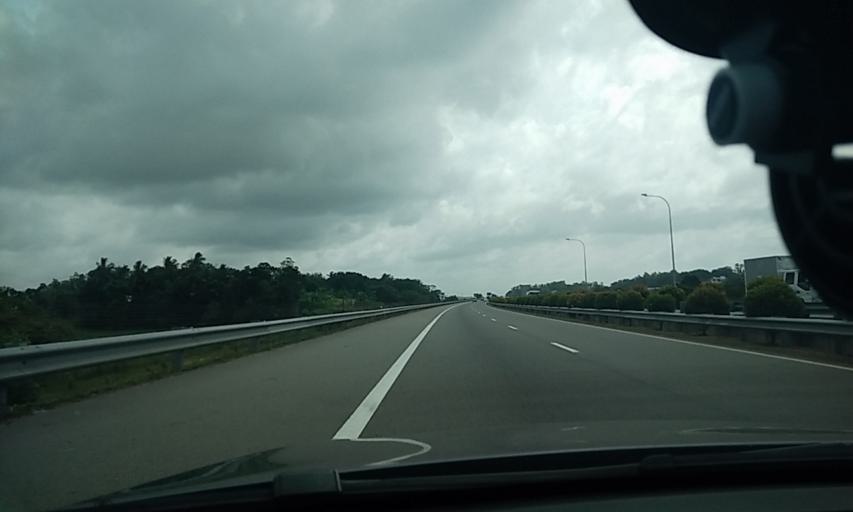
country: LK
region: Western
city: Homagama
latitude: 6.8879
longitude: 79.9770
